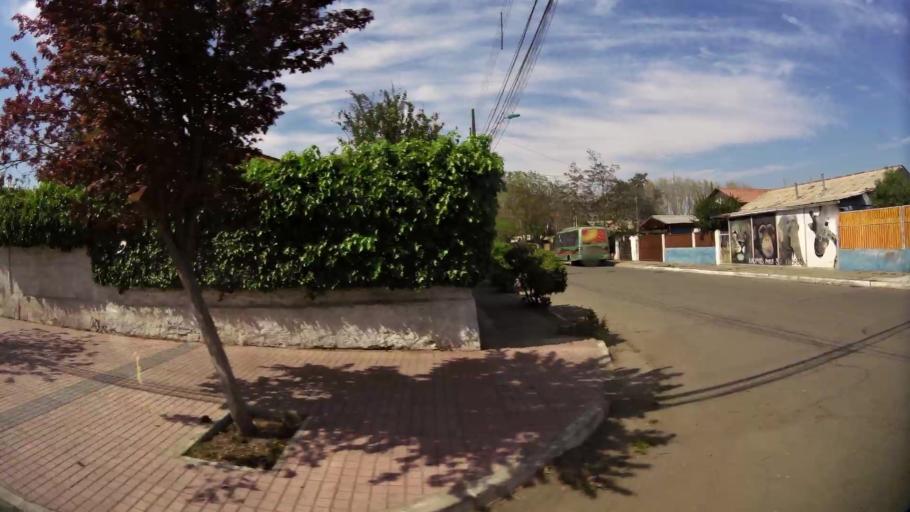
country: CL
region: Santiago Metropolitan
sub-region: Provincia de Talagante
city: Talagante
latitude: -33.6672
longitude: -70.9237
